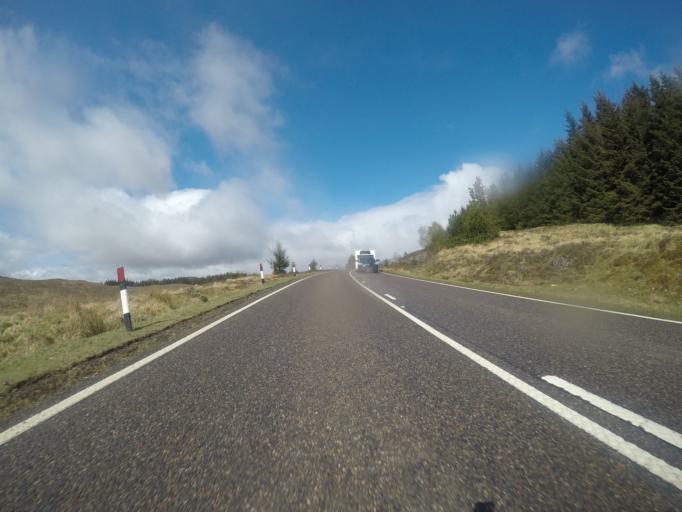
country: GB
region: Scotland
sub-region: Highland
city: Spean Bridge
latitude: 57.0936
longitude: -4.9908
